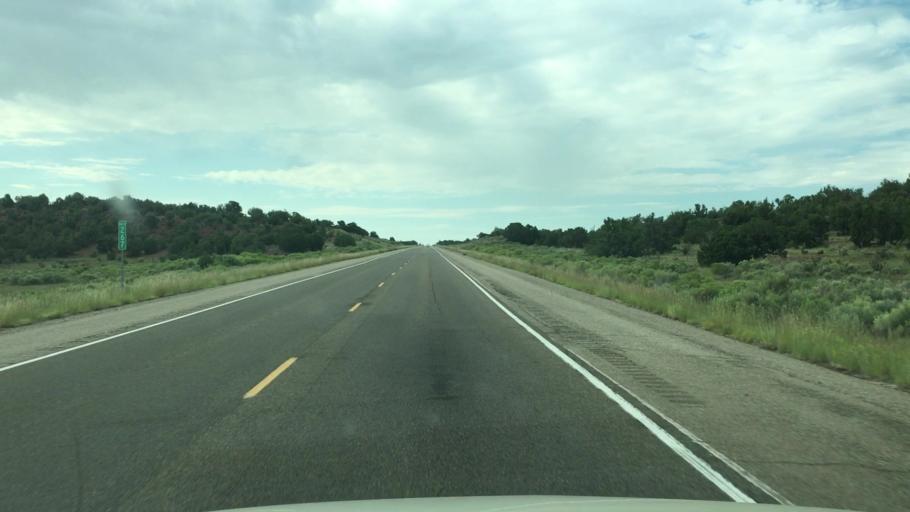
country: US
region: New Mexico
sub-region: Santa Fe County
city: Eldorado at Santa Fe
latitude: 35.2362
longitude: -105.8044
